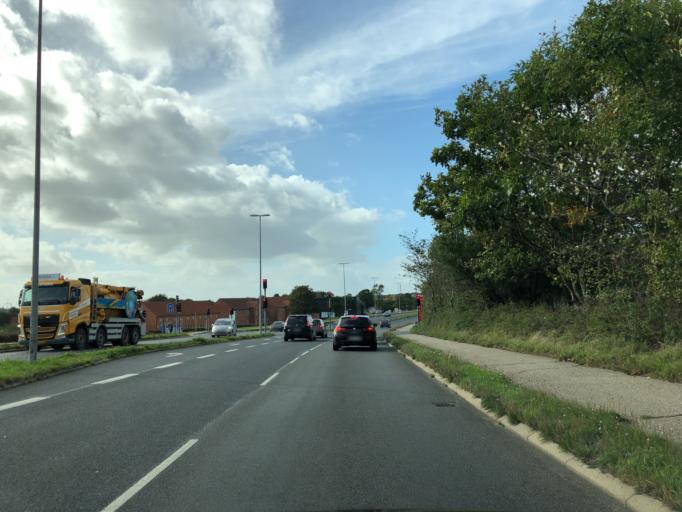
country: DK
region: Central Jutland
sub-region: Holstebro Kommune
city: Holstebro
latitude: 56.3599
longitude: 8.6029
